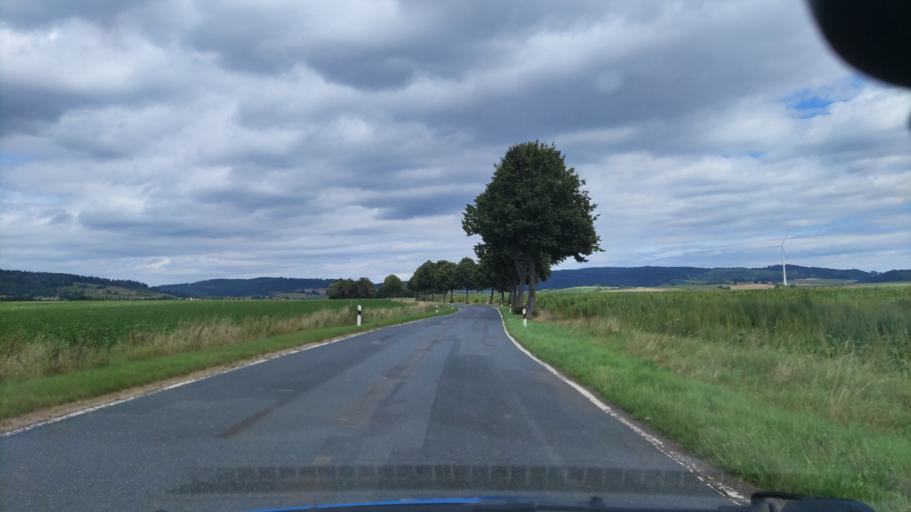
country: DE
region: Lower Saxony
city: Dassel
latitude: 51.8267
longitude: 9.7177
